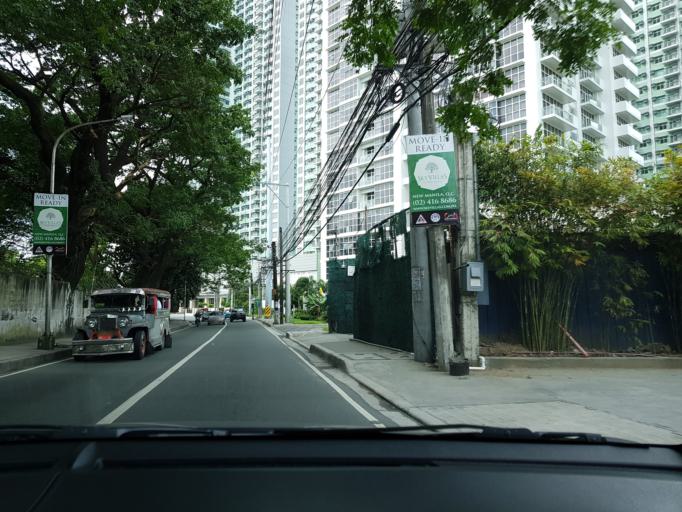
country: PH
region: Metro Manila
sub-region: San Juan
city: San Juan
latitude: 14.6151
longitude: 121.0404
